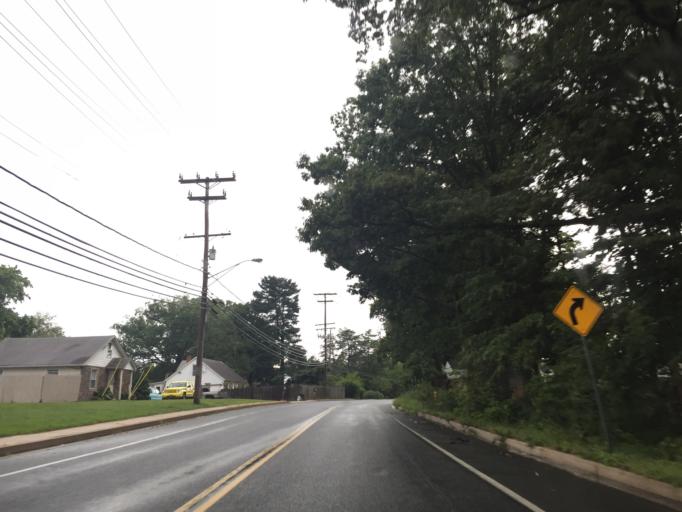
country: US
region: Maryland
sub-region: Harford County
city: Bel Air South
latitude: 39.4750
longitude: -76.3051
